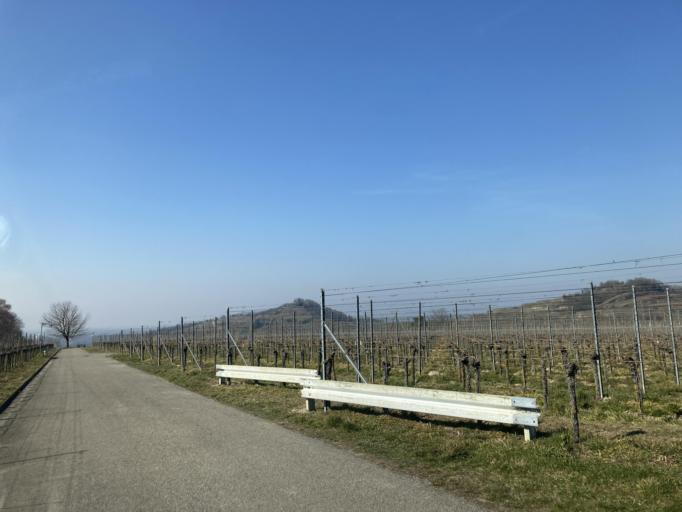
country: DE
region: Baden-Wuerttemberg
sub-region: Freiburg Region
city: Ihringen
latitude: 48.0643
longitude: 7.6394
